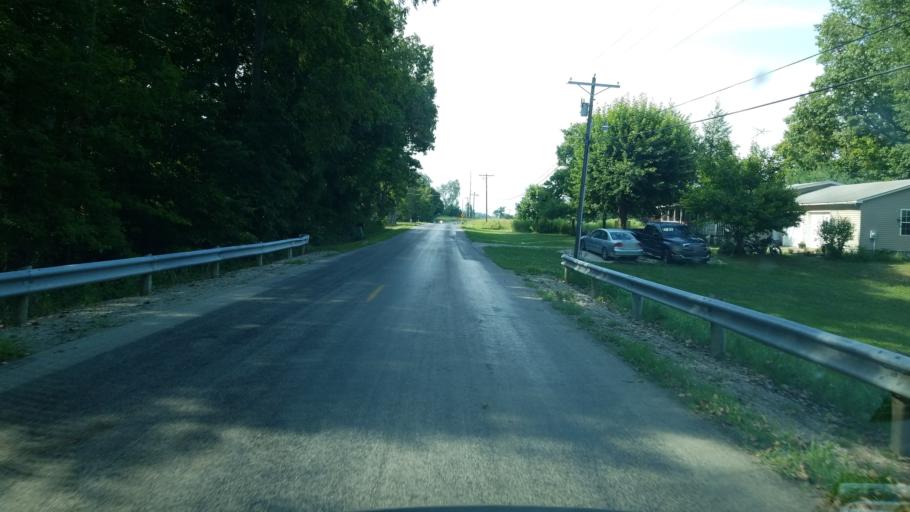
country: US
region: Ohio
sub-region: Marion County
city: Prospect
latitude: 40.5260
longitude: -83.2139
